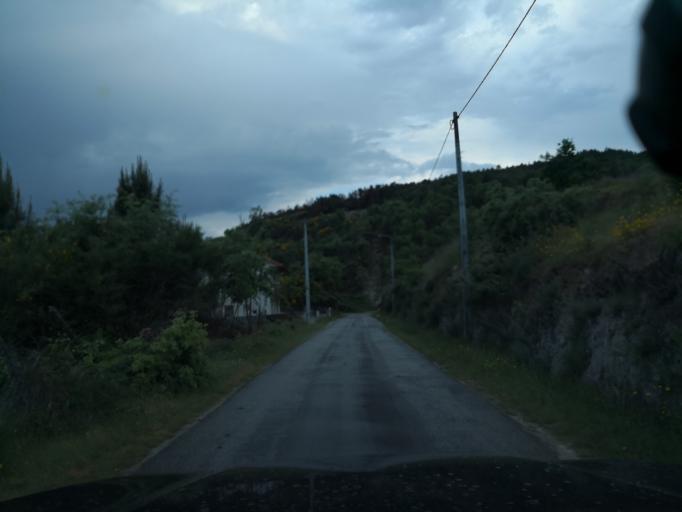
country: PT
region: Vila Real
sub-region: Vila Real
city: Vila Real
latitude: 41.3560
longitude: -7.7296
